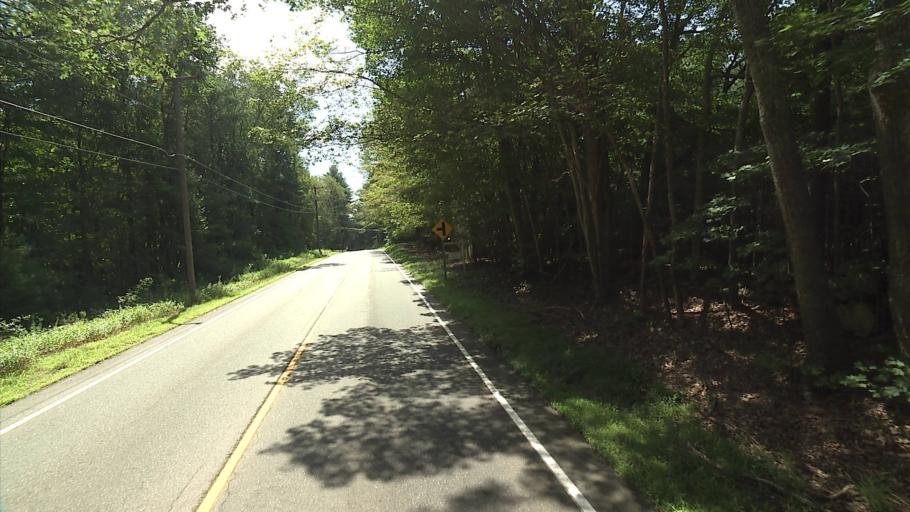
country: US
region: Connecticut
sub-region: Windham County
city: South Woodstock
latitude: 41.9594
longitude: -72.0790
